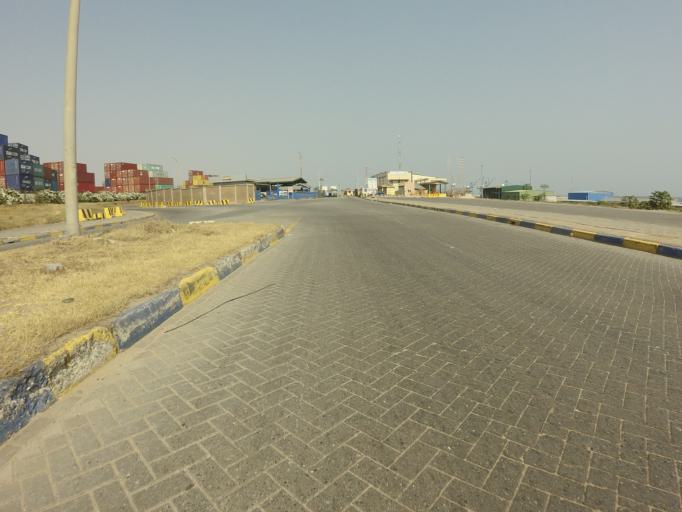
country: GH
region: Greater Accra
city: Tema
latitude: 5.6241
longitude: -0.0069
